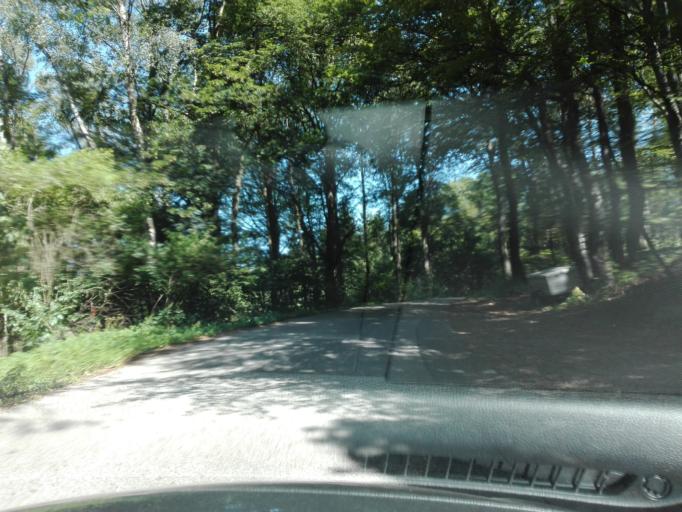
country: AT
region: Upper Austria
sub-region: Politischer Bezirk Urfahr-Umgebung
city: Steyregg
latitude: 48.2973
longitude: 14.3718
